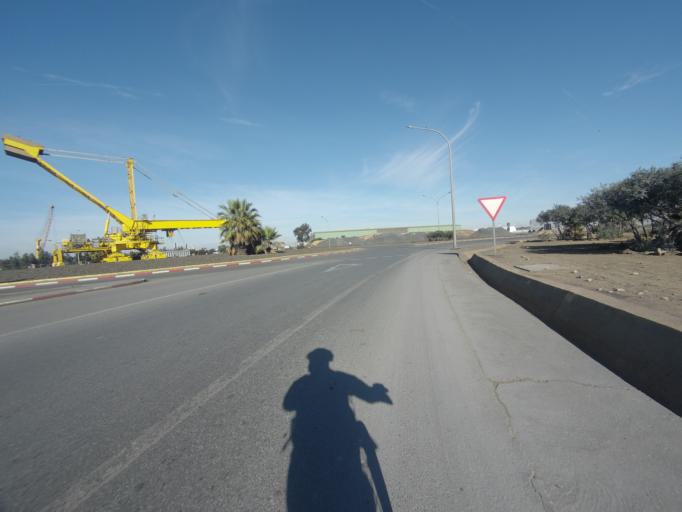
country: ES
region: Andalusia
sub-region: Provincia de Huelva
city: Punta Umbria
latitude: 37.1911
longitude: -6.9301
